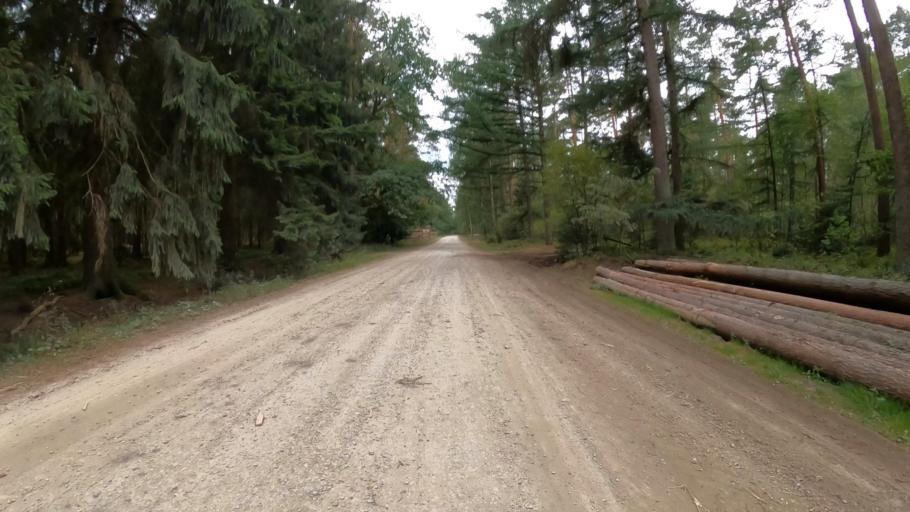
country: DE
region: Lower Saxony
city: Kakenstorf
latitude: 53.3128
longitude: 9.7366
